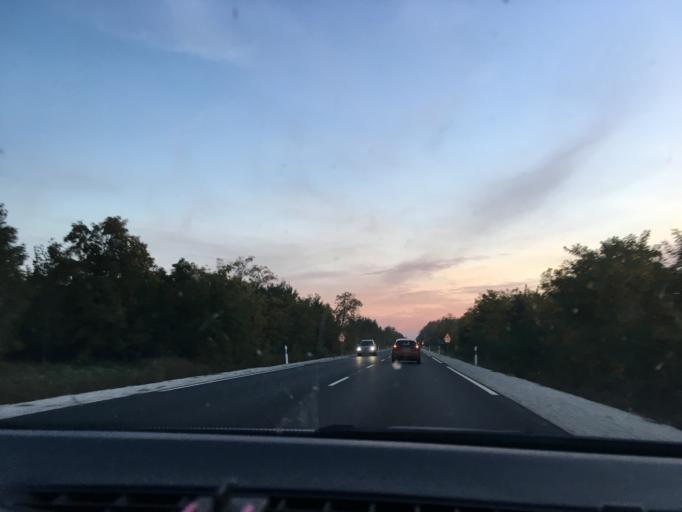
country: HU
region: Hajdu-Bihar
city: Hajduhadhaz
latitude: 47.6197
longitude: 21.6593
